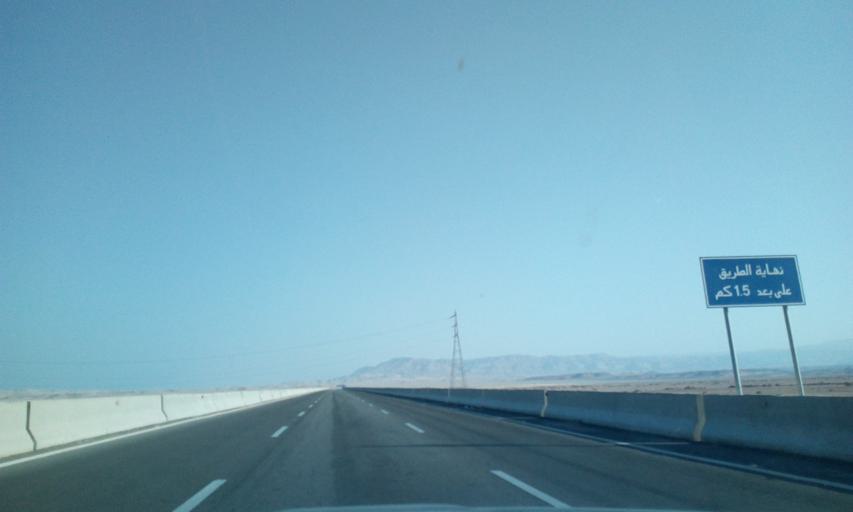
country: EG
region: As Suways
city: Ain Sukhna
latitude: 29.1226
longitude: 32.5275
